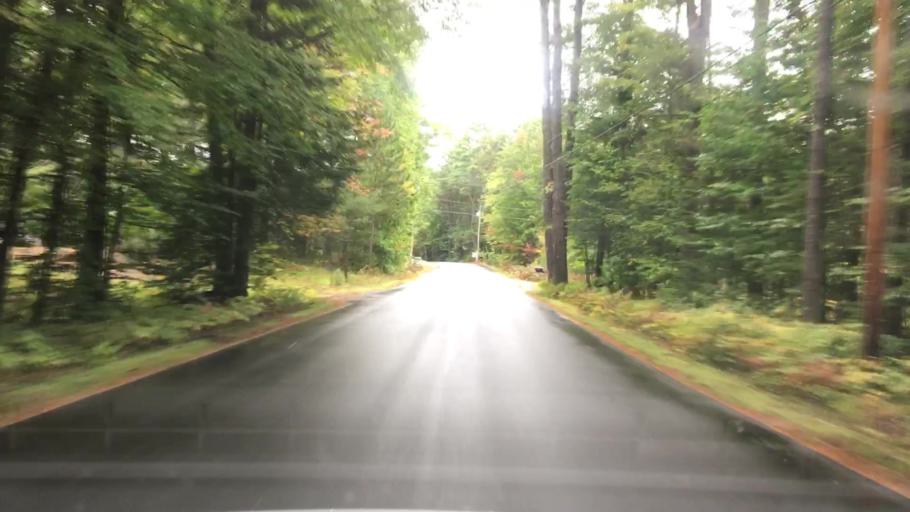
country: US
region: Maine
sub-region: Cumberland County
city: Raymond
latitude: 43.9948
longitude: -70.5667
